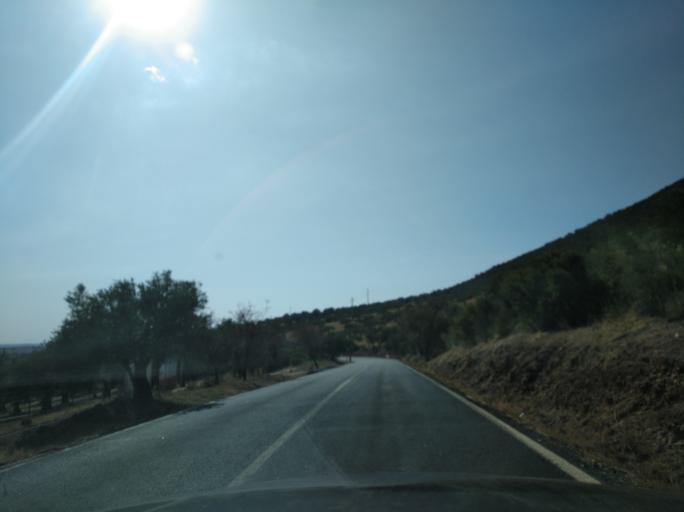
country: ES
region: Andalusia
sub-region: Provincia de Huelva
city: Rosal de la Frontera
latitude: 37.9551
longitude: -7.2738
